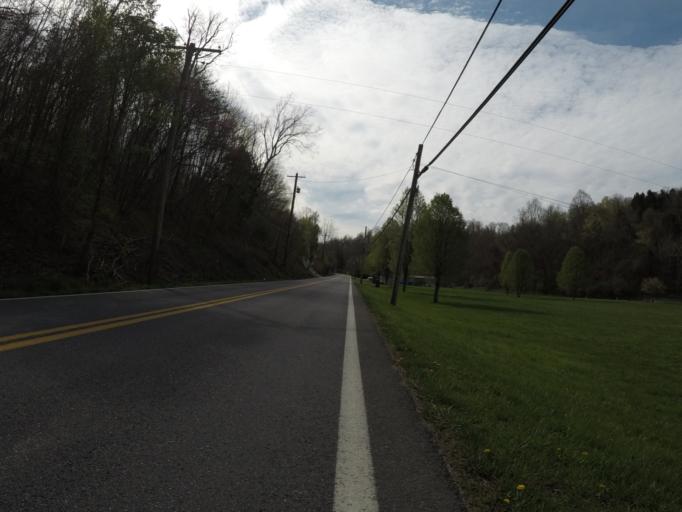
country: US
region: West Virginia
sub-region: Cabell County
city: Pea Ridge
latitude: 38.3798
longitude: -82.3745
